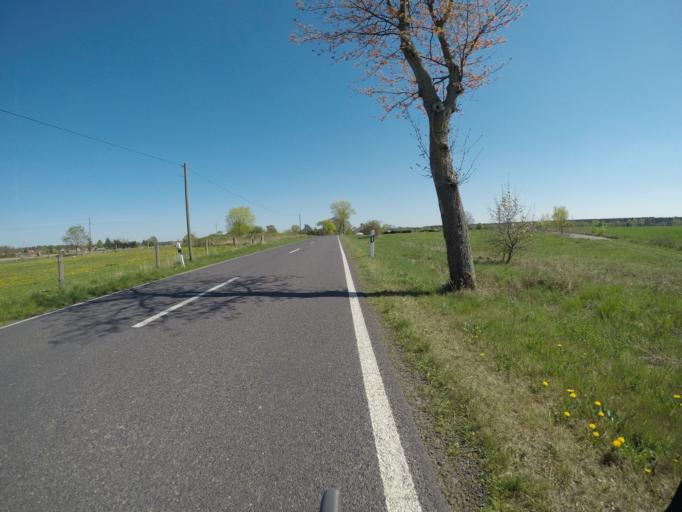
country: DE
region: Brandenburg
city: Strausberg
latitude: 52.6120
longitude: 13.8606
